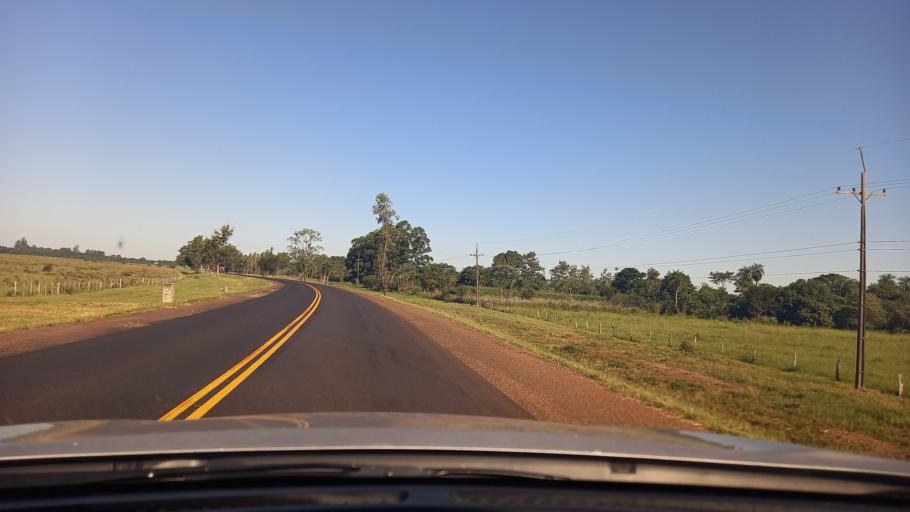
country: PY
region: Itapua
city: General Delgado
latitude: -27.1103
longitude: -56.4232
